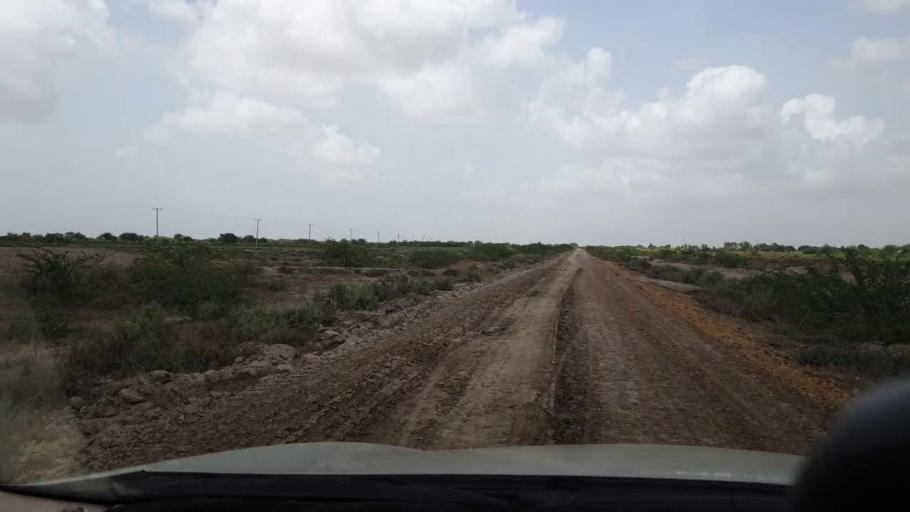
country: PK
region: Sindh
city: Kadhan
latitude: 24.3740
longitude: 68.8569
